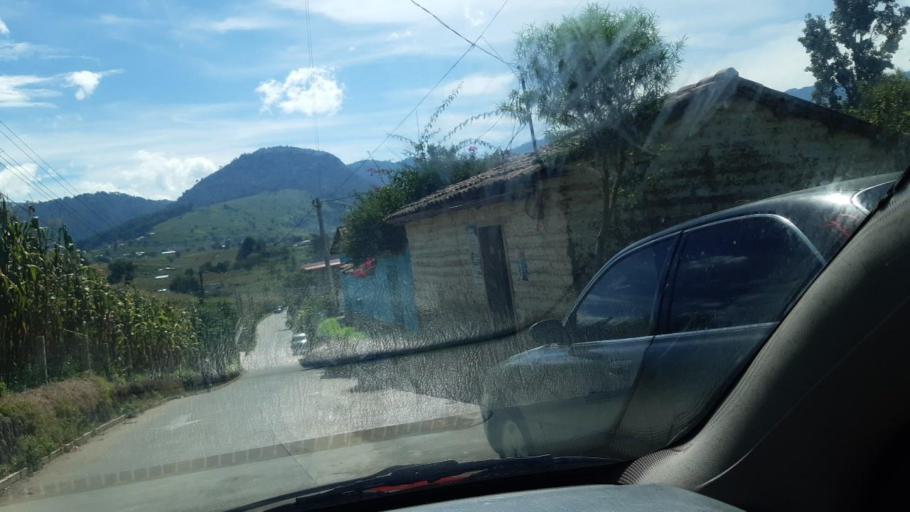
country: GT
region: Quetzaltenango
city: Salcaja
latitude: 14.8760
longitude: -91.4465
